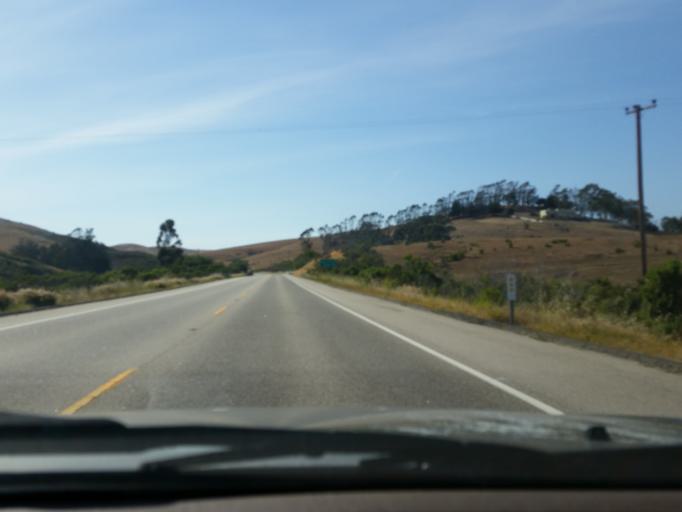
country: US
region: California
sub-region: San Luis Obispo County
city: Cayucos
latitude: 35.4670
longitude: -120.9746
